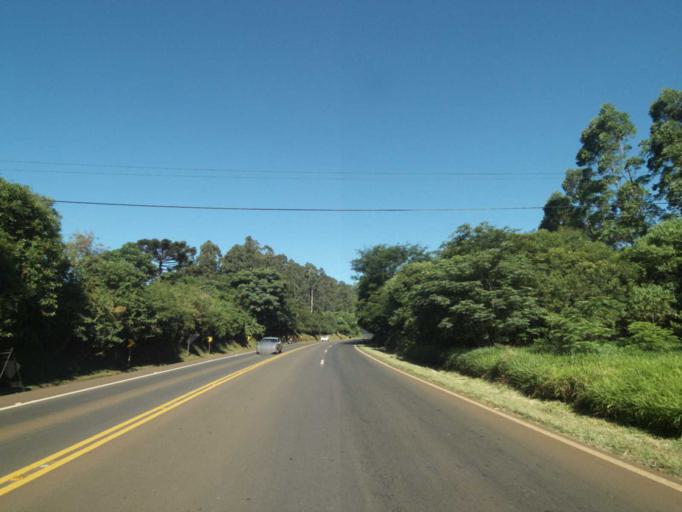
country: BR
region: Parana
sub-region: Laranjeiras Do Sul
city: Laranjeiras do Sul
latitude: -25.3781
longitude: -52.1997
